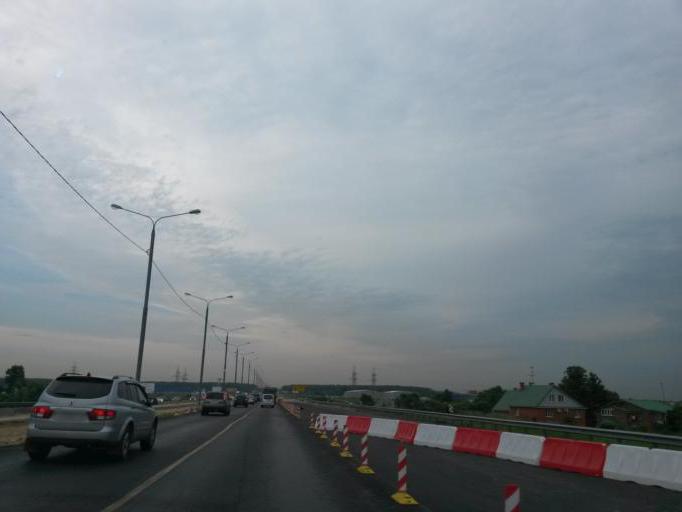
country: RU
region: Moskovskaya
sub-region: Podol'skiy Rayon
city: Podol'sk
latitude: 55.3806
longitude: 37.6050
